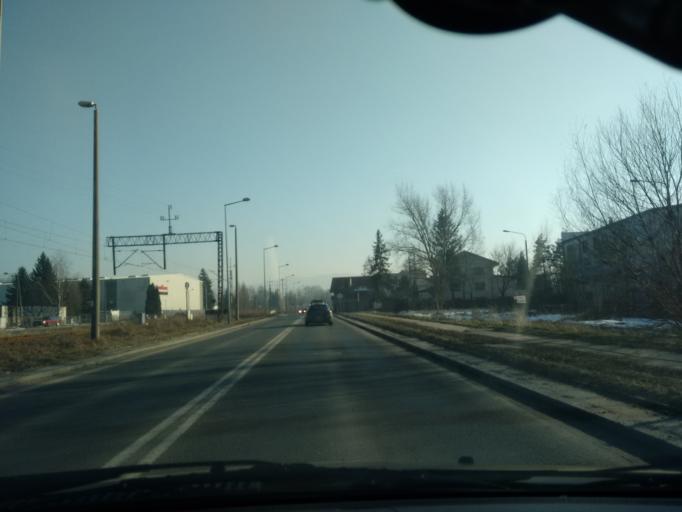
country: PL
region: Lesser Poland Voivodeship
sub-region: Powiat wadowicki
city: Wadowice
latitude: 49.8811
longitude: 19.5053
